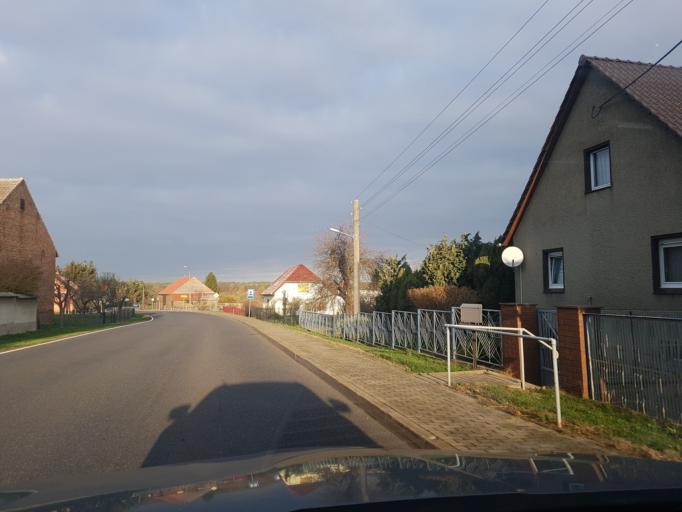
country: DE
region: Brandenburg
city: Kasel-Golzig
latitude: 51.8993
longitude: 13.6788
